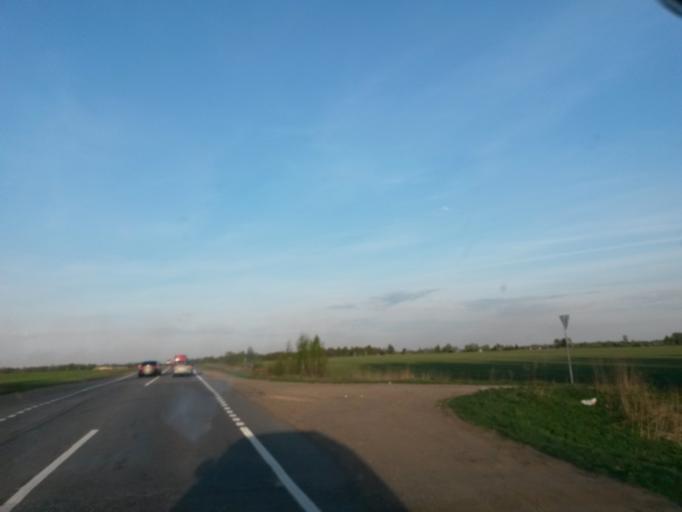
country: RU
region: Jaroslavl
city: Kurba
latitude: 57.6820
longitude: 39.5084
